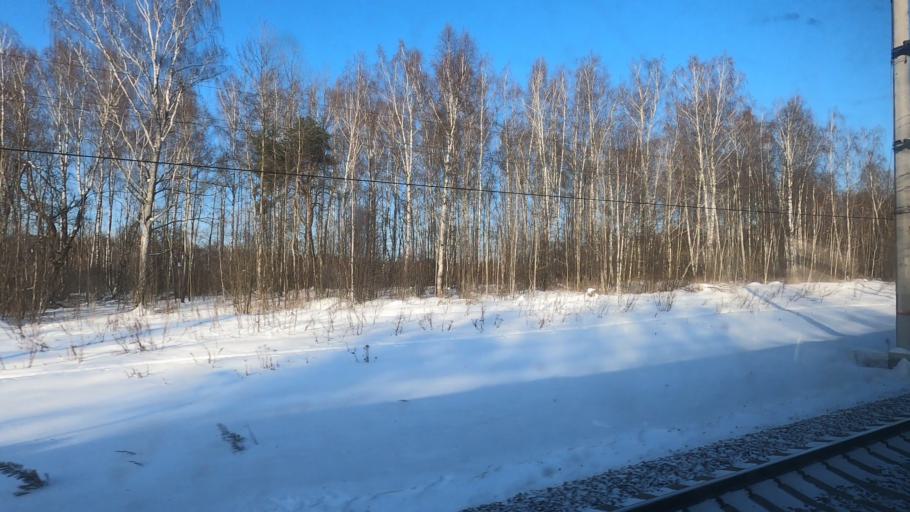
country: RU
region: Moskovskaya
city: Rakhmanovo
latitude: 55.7501
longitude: 38.5437
